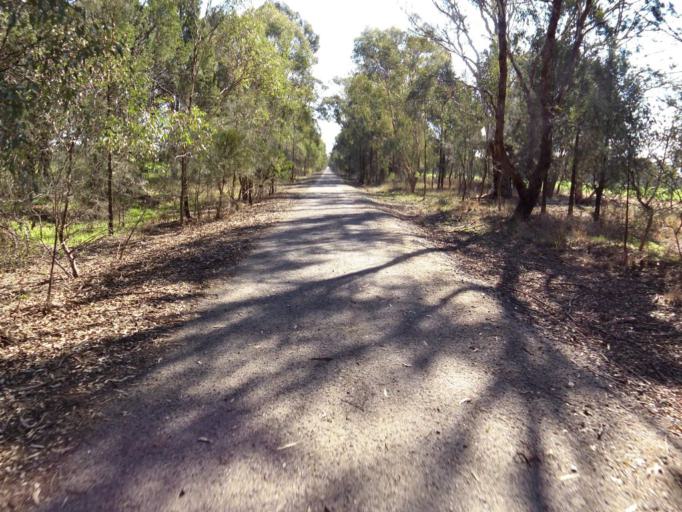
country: AU
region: New South Wales
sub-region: Corowa Shire
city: Corowa
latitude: -36.0313
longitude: 146.4422
